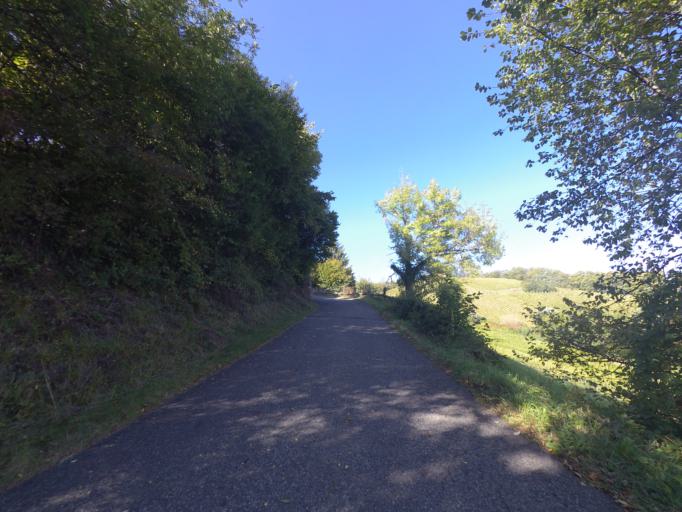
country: AT
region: Styria
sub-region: Politischer Bezirk Leibnitz
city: Kitzeck im Sausal
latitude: 46.7765
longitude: 15.4333
